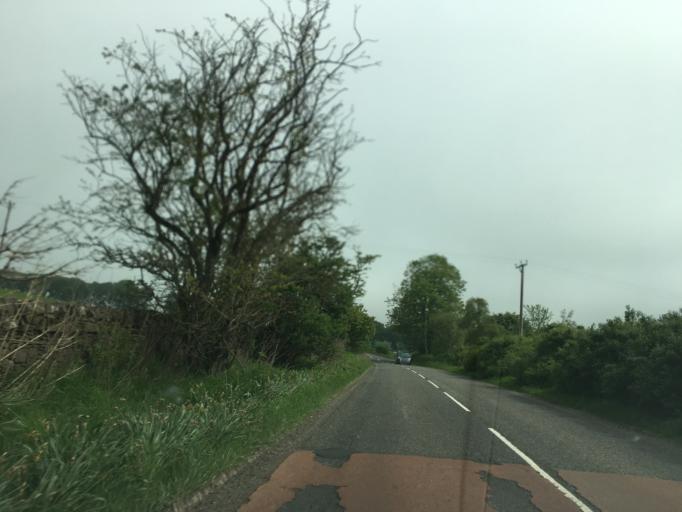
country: GB
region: Scotland
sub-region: The Scottish Borders
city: West Linton
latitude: 55.7089
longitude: -3.3529
